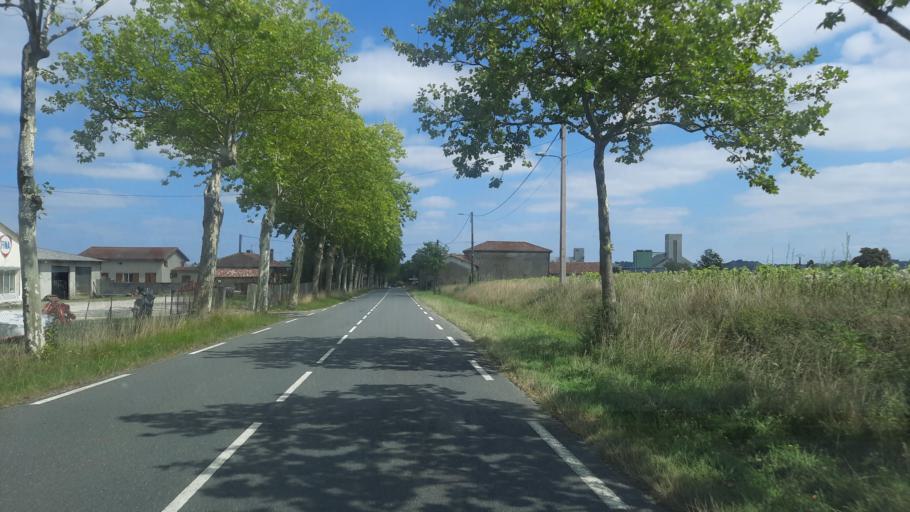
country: FR
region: Midi-Pyrenees
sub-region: Departement de la Haute-Garonne
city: Boulogne-sur-Gesse
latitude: 43.2928
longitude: 0.6541
